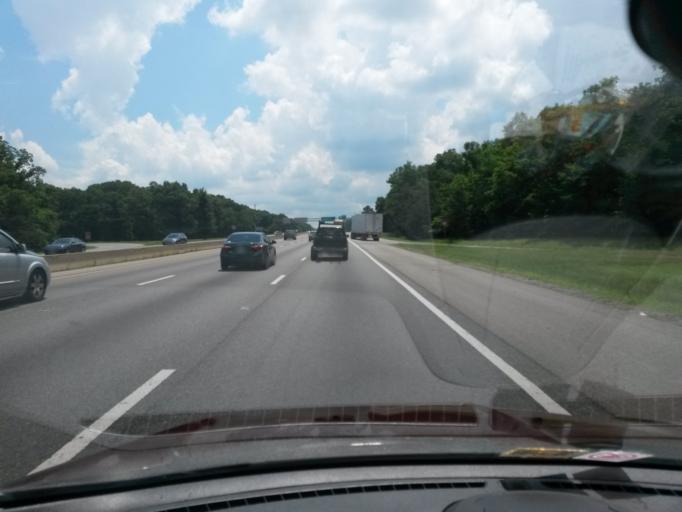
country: US
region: Virginia
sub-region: Chesterfield County
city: Chester
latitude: 37.3578
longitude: -77.4044
